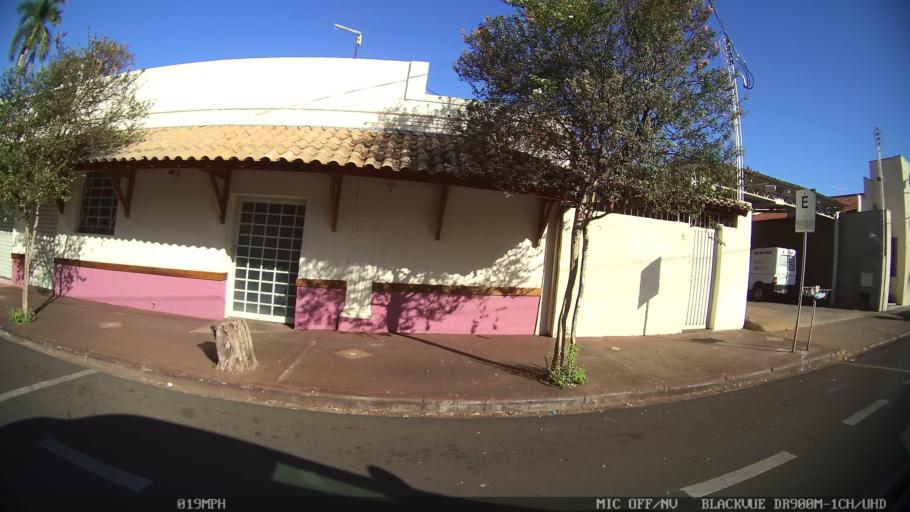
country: BR
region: Sao Paulo
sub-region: Olimpia
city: Olimpia
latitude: -20.7381
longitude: -48.9162
